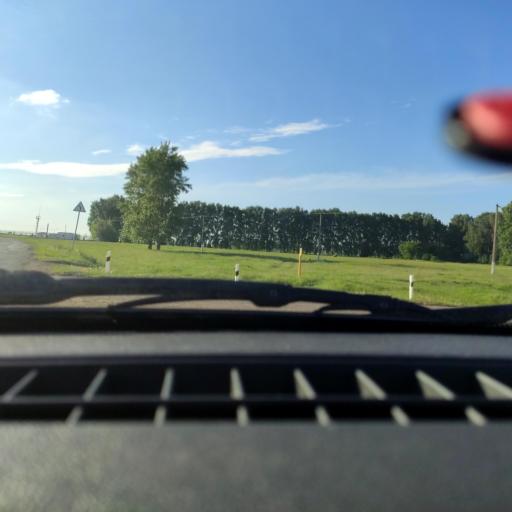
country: RU
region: Bashkortostan
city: Tolbazy
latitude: 54.2948
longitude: 55.8073
